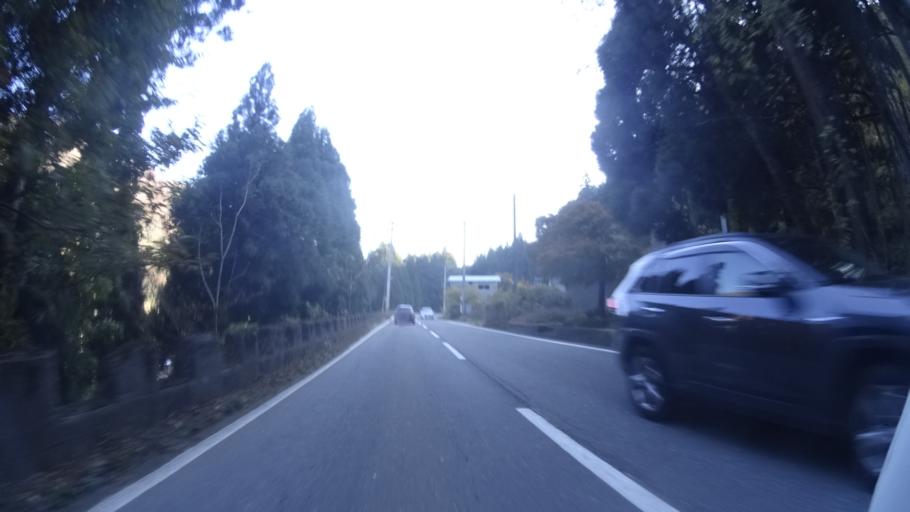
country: JP
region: Fukui
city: Ono
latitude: 35.9673
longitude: 136.5949
